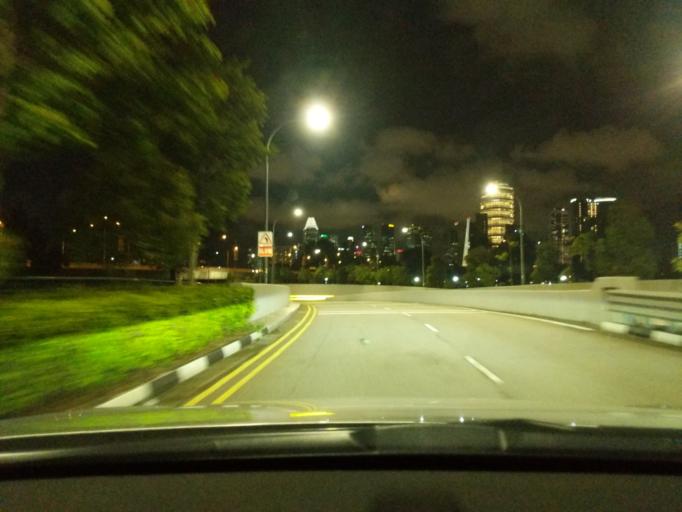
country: SG
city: Singapore
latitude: 1.3061
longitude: 103.8697
